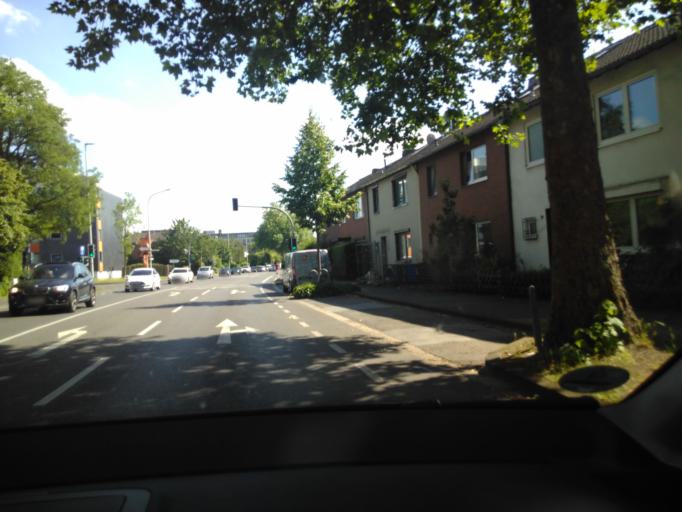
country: DE
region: North Rhine-Westphalia
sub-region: Regierungsbezirk Dusseldorf
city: Hilden
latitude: 51.1740
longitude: 6.9400
